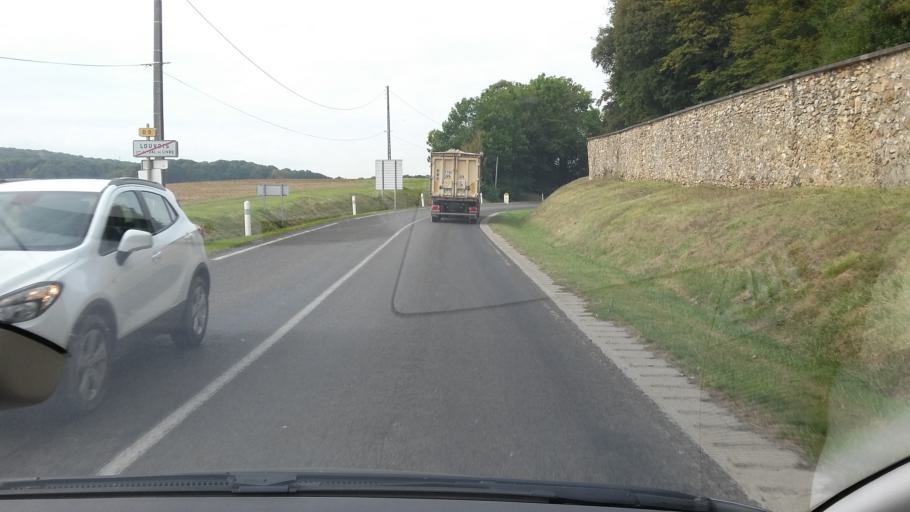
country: FR
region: Champagne-Ardenne
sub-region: Departement de la Marne
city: Tours-sur-Marne
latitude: 49.1043
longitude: 4.1166
